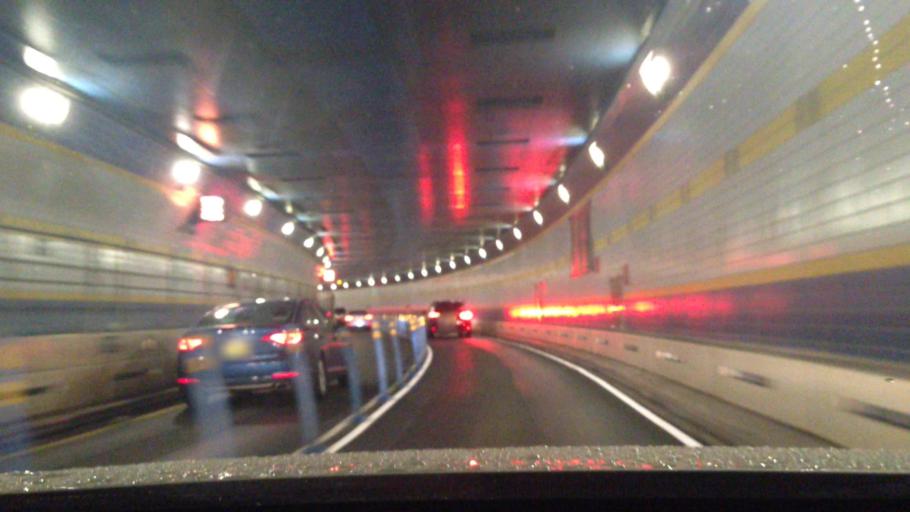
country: US
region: New York
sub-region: Queens County
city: Long Island City
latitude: 40.7444
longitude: -73.9667
